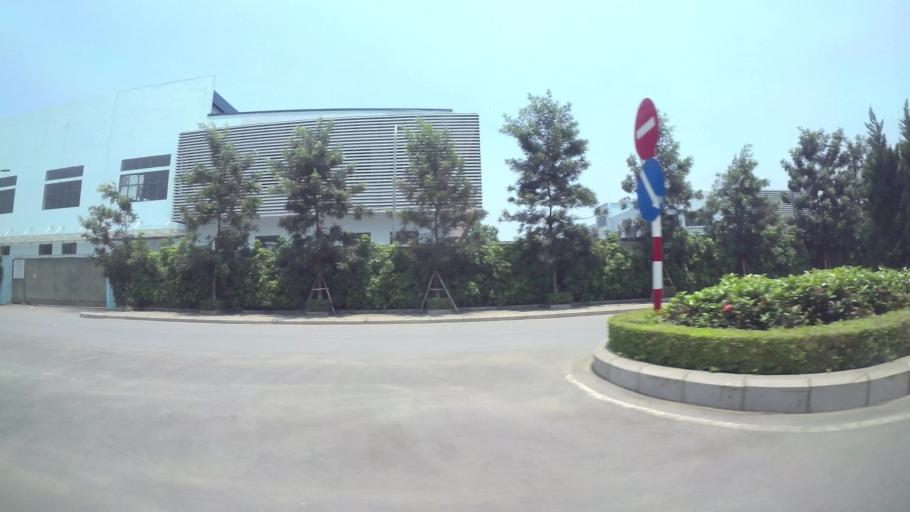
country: VN
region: Ha Noi
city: Trau Quy
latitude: 21.0320
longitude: 105.8996
